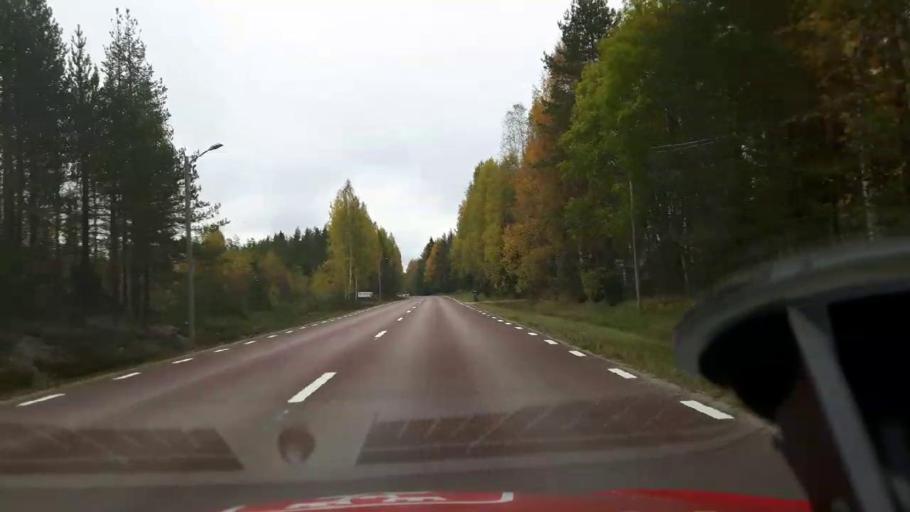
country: SE
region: Jaemtland
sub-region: Harjedalens Kommun
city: Sveg
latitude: 62.3117
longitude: 14.7567
